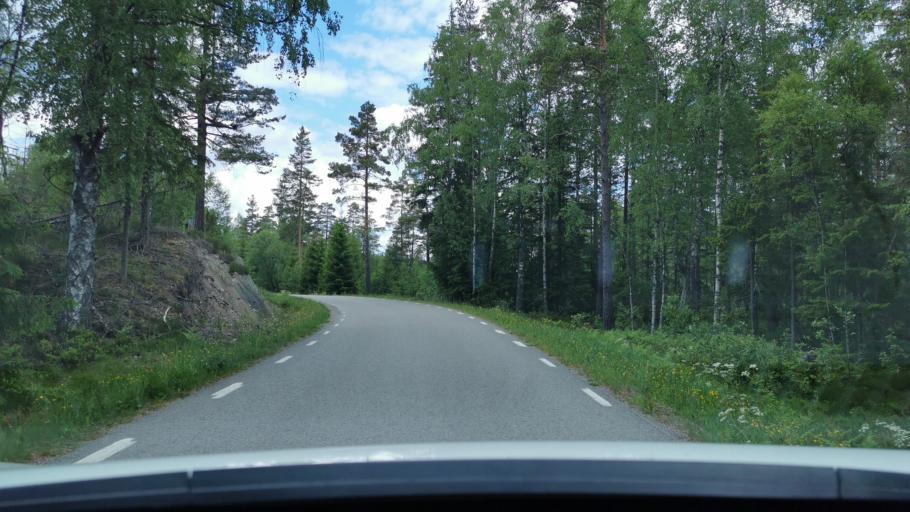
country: SE
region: Vaestra Goetaland
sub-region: Bengtsfors Kommun
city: Dals Langed
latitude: 58.8561
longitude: 12.3300
